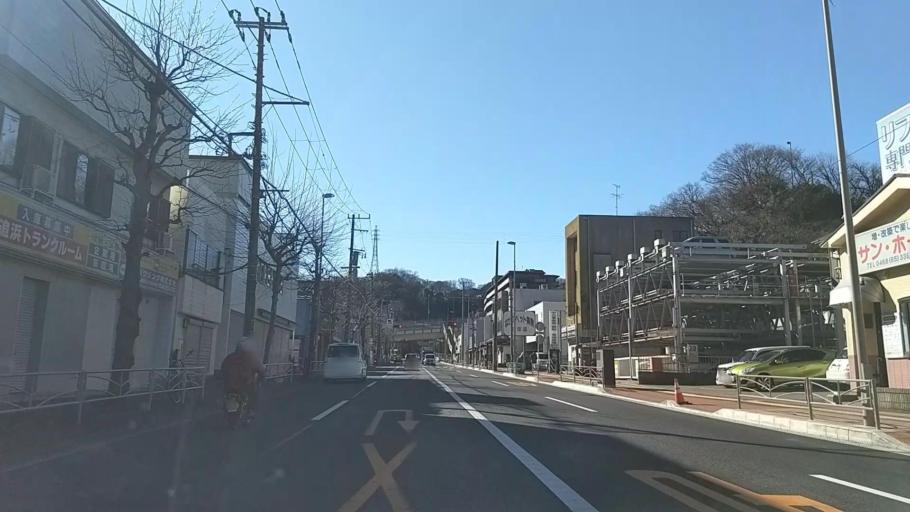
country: JP
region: Kanagawa
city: Zushi
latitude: 35.3097
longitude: 139.6243
